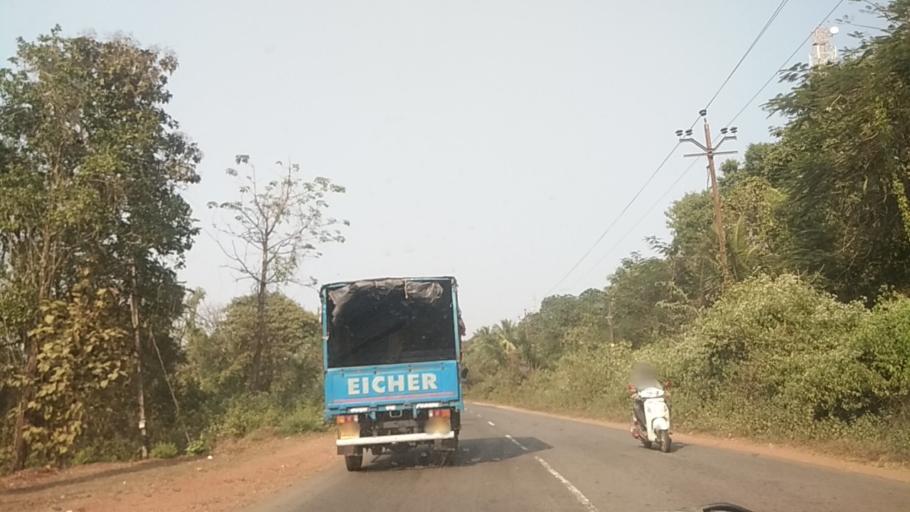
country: IN
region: Goa
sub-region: North Goa
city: Colovale
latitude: 15.6435
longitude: 73.8346
